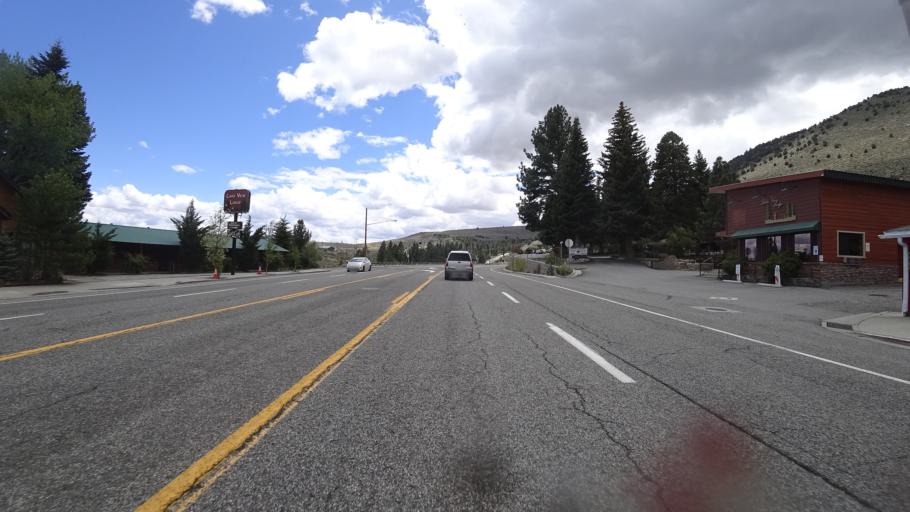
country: US
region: California
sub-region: Mono County
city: Bridgeport
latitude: 37.9556
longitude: -119.1187
